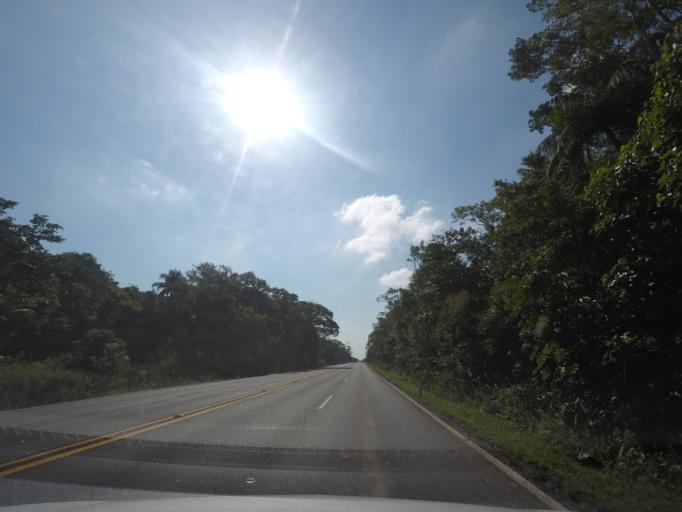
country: BR
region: Parana
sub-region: Pontal Do Parana
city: Pontal do Parana
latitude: -25.6418
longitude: -48.5911
